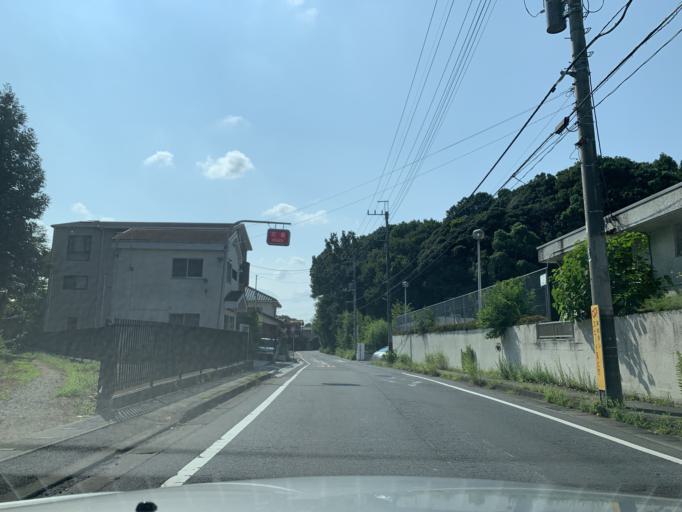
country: JP
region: Chiba
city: Kashiwa
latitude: 35.8420
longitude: 139.9410
